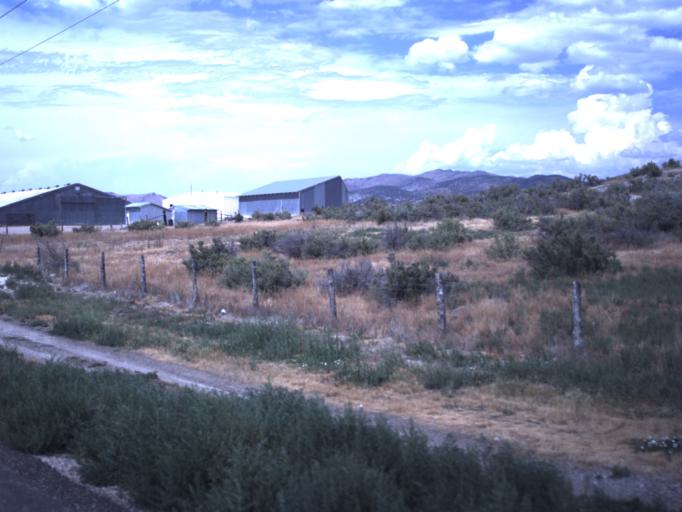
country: US
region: Utah
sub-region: Sanpete County
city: Moroni
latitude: 39.5424
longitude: -111.5960
